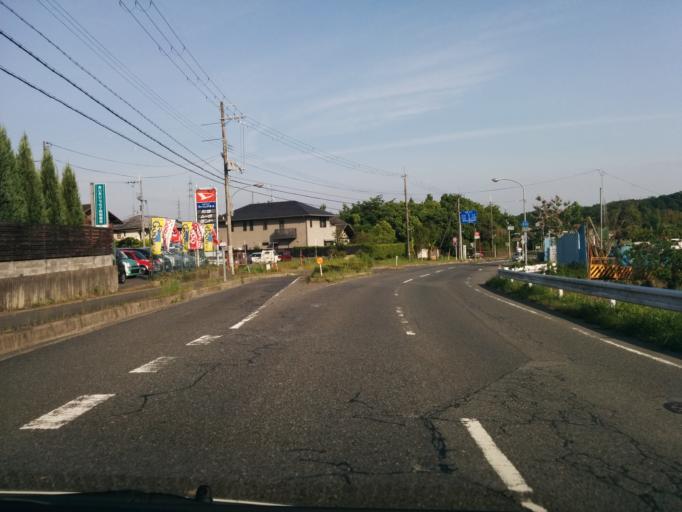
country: JP
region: Shiga Prefecture
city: Kitahama
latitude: 35.1005
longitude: 135.8884
